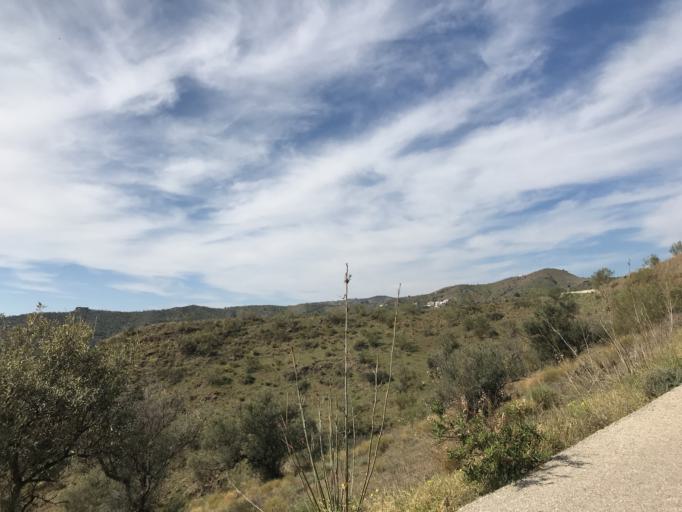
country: ES
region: Andalusia
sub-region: Provincia de Malaga
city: Valdes
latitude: 36.7740
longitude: -4.2161
